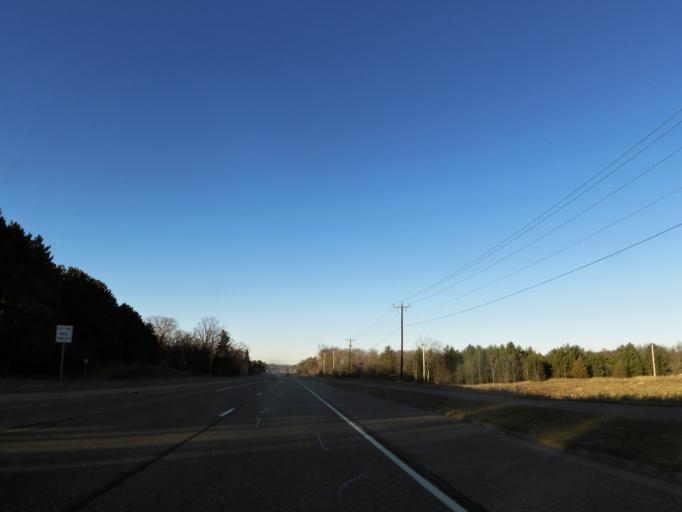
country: US
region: Minnesota
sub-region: Washington County
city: Lake Elmo
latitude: 45.0439
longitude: -92.8629
